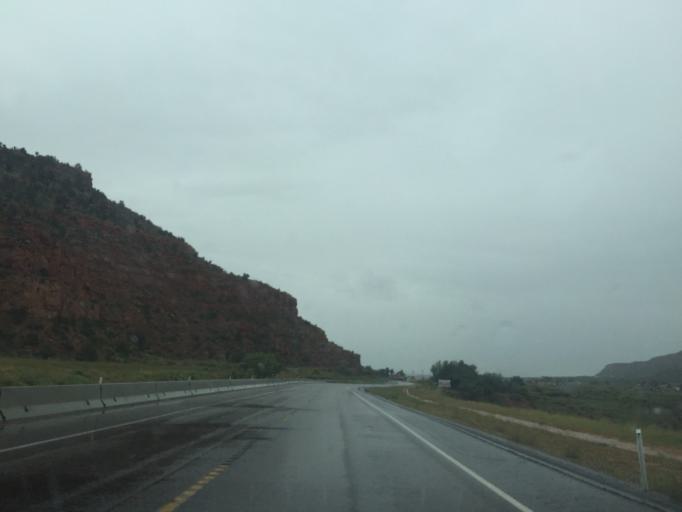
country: US
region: Utah
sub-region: Kane County
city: Kanab
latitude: 37.0642
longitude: -112.5370
